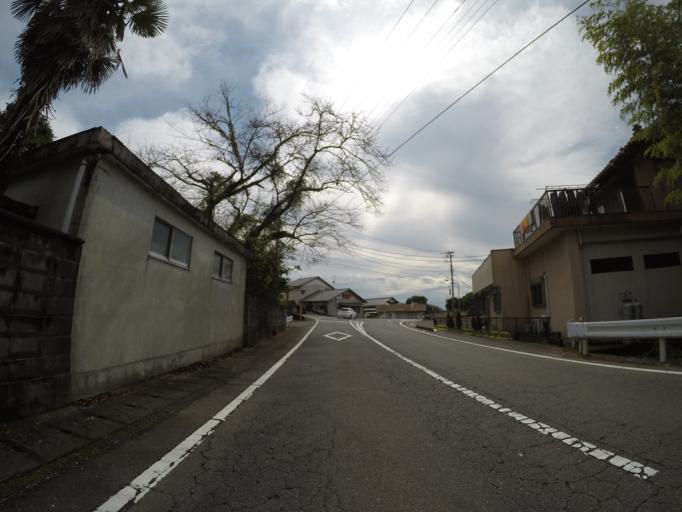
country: JP
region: Shizuoka
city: Fuji
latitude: 35.2243
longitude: 138.6901
